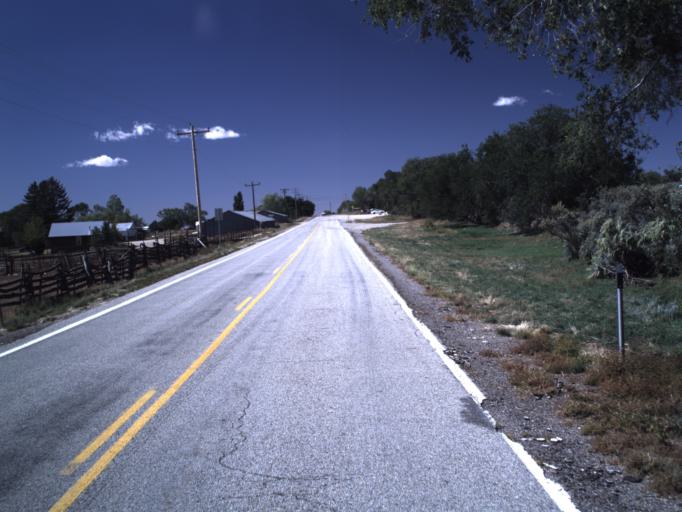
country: US
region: Utah
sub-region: Grand County
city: Moab
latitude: 38.3124
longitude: -109.2464
